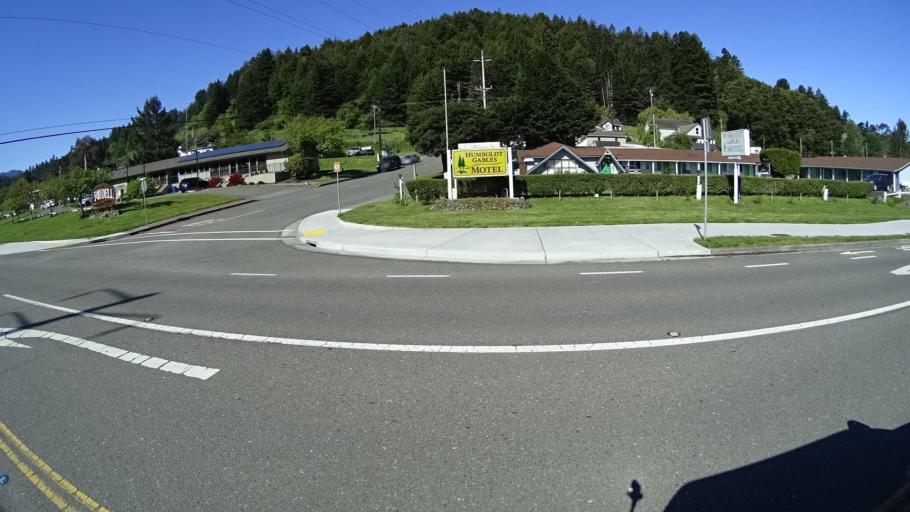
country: US
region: California
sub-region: Humboldt County
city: Rio Dell
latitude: 40.4993
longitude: -124.1062
